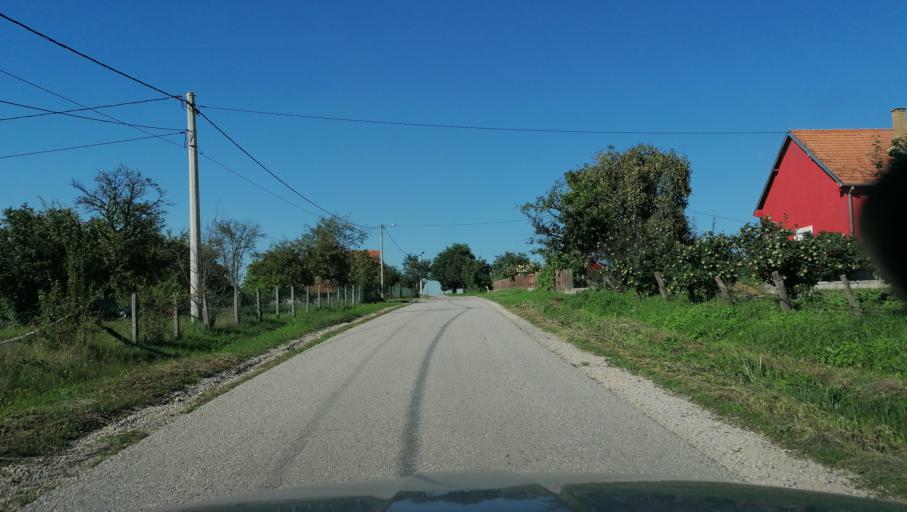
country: RS
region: Central Serbia
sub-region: Sumadijski Okrug
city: Knic
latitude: 43.8725
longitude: 20.6097
